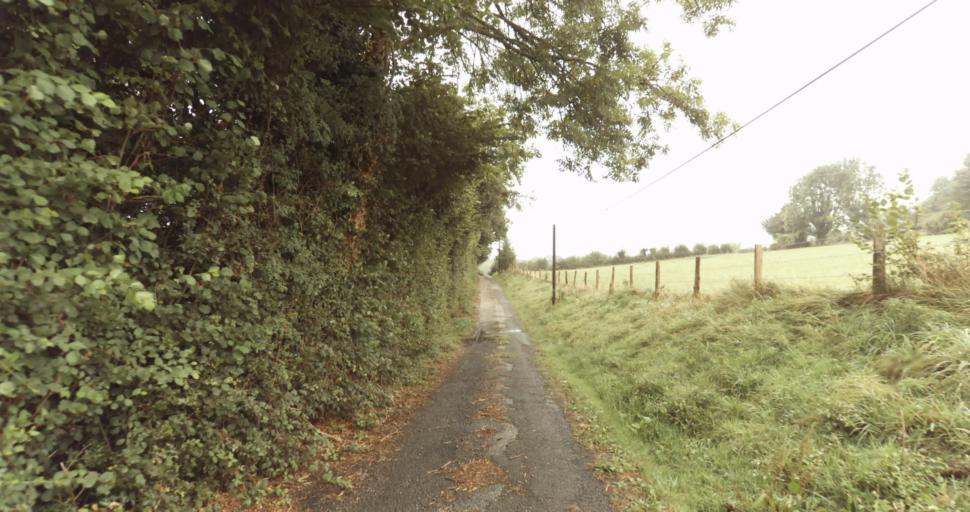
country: FR
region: Lower Normandy
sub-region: Departement de l'Orne
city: Vimoutiers
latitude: 48.8692
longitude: 0.2044
